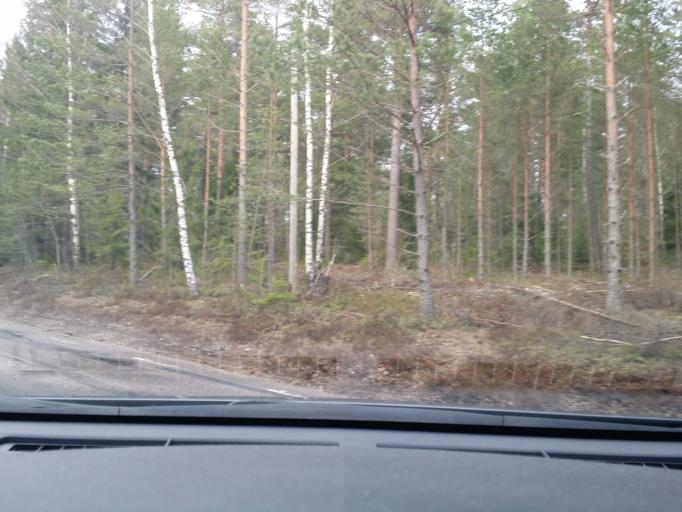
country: SE
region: Soedermanland
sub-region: Eskilstuna Kommun
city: Arla
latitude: 59.2990
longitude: 16.6764
